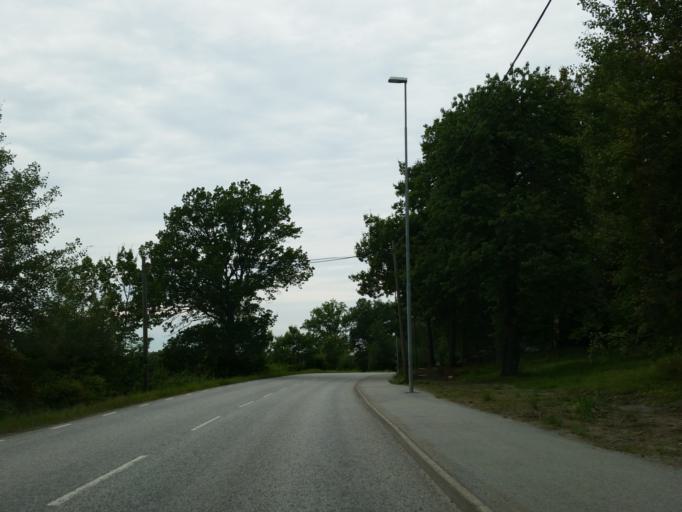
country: SE
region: Stockholm
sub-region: Botkyrka Kommun
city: Eriksberg
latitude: 59.2396
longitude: 17.8113
